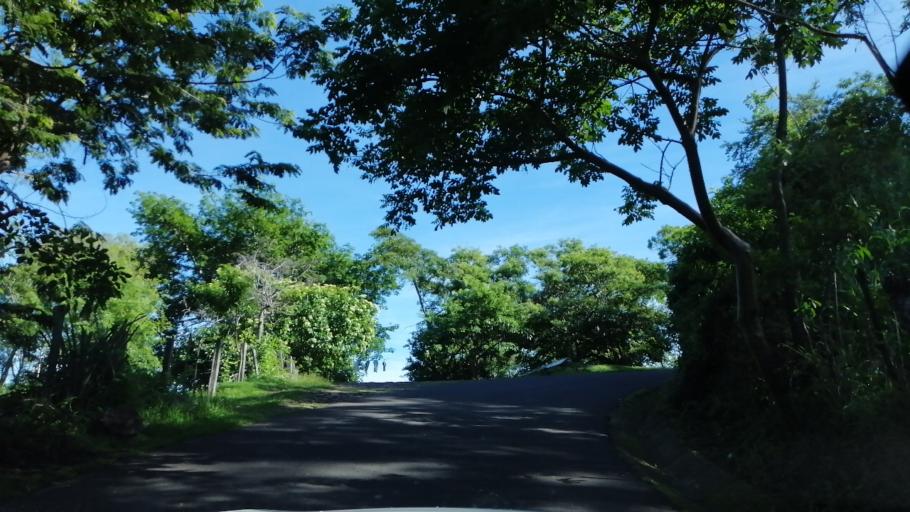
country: SV
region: Morazan
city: Corinto
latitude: 13.8043
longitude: -88.0044
